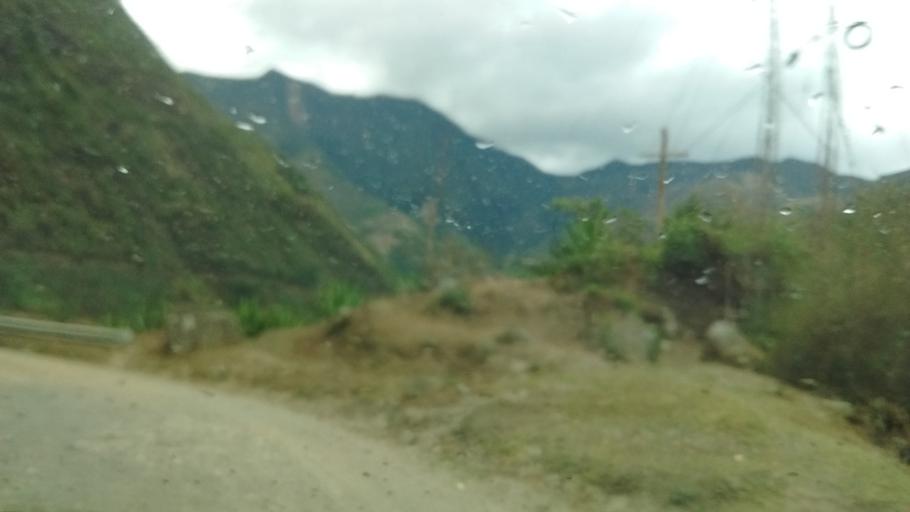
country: CO
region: Cauca
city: La Vega
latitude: 2.0370
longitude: -76.7981
